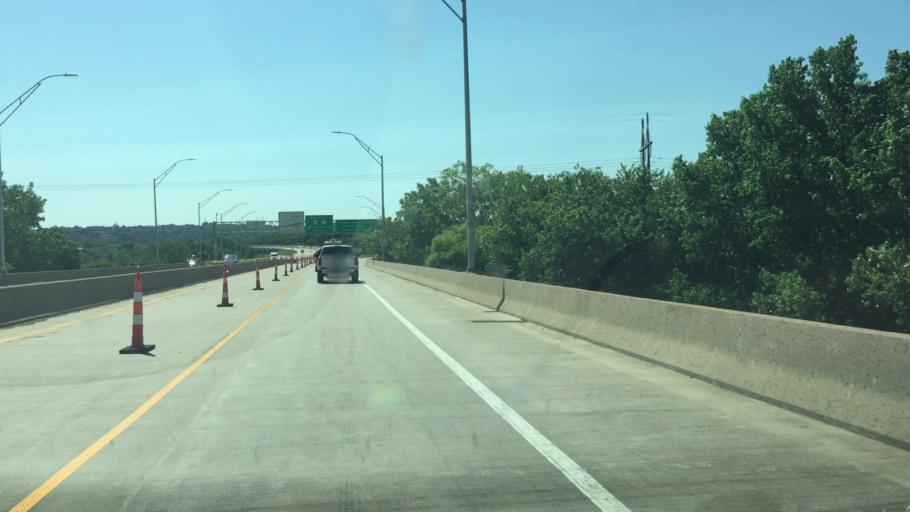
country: US
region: Illinois
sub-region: Jo Daviess County
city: East Dubuque
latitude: 42.5157
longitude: -90.6402
